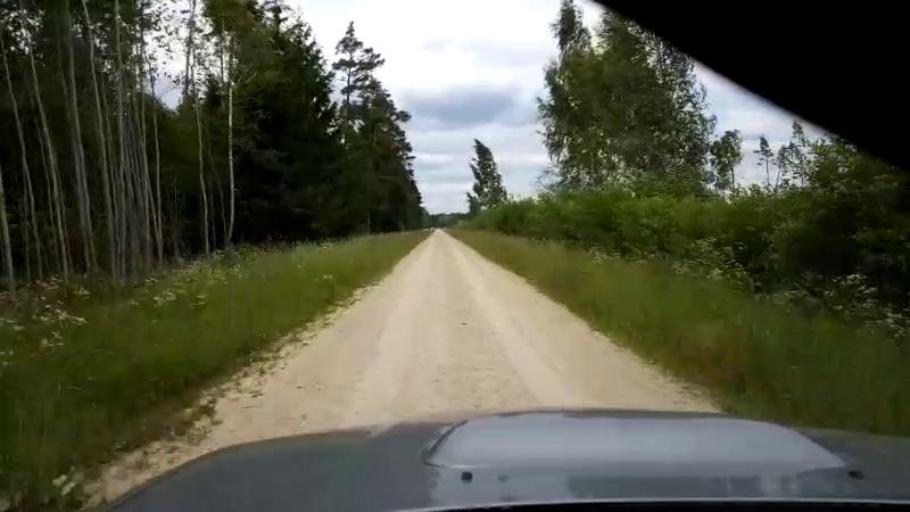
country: EE
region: Paernumaa
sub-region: Sauga vald
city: Sauga
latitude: 58.5078
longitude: 24.5806
